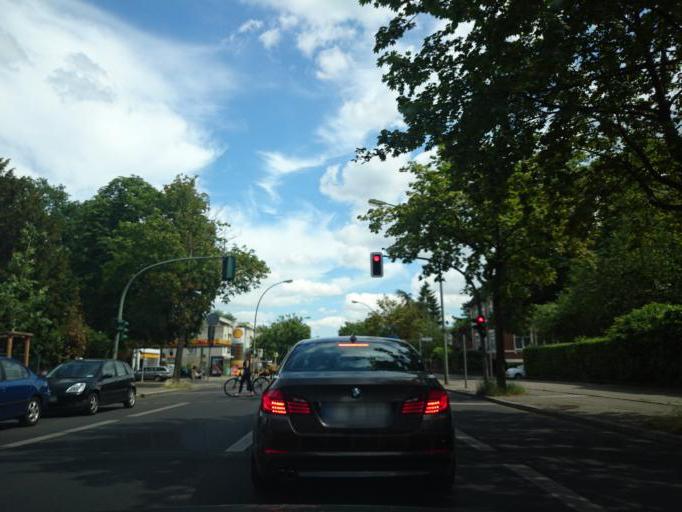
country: DE
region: Berlin
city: Lichterfelde
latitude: 52.4298
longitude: 13.3207
